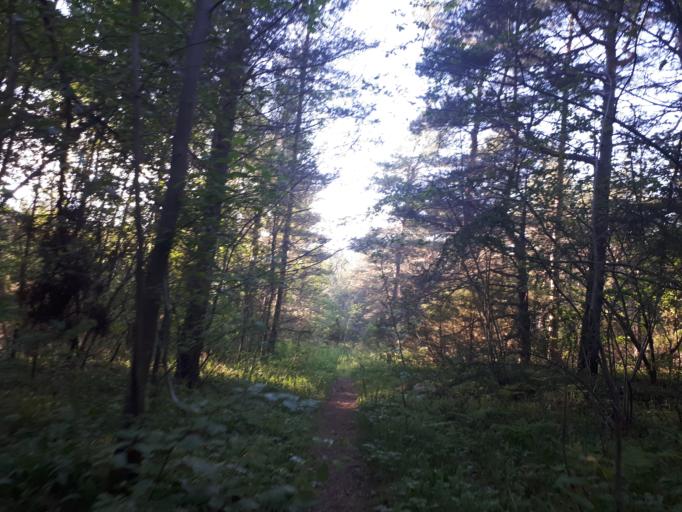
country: SE
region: Gotland
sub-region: Gotland
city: Visby
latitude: 57.6070
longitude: 18.2886
